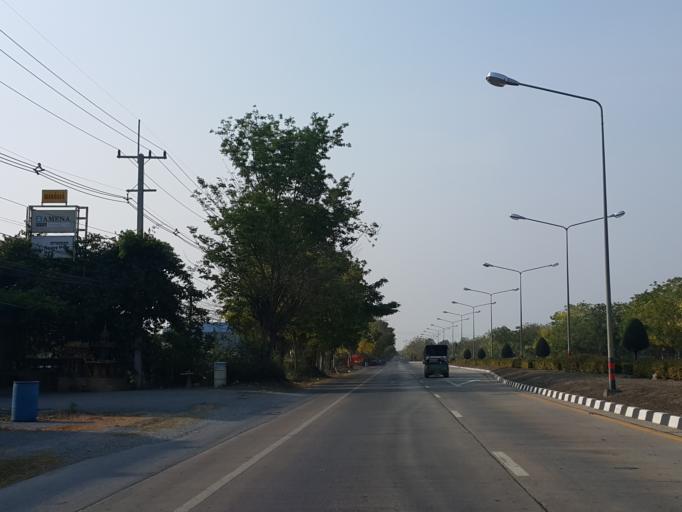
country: TH
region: Suphan Buri
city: Sam Chuk
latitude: 14.7694
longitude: 100.0920
